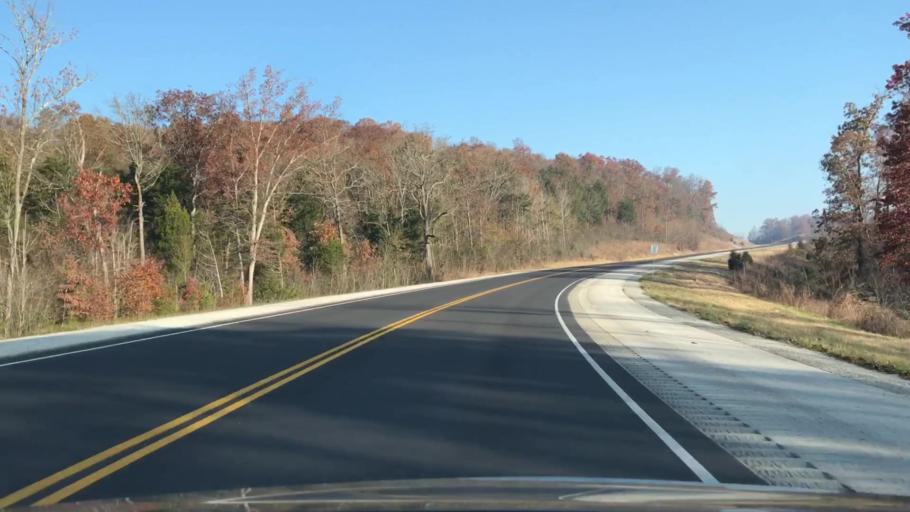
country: US
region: Kentucky
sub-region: Edmonson County
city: Brownsville
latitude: 37.0945
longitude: -86.2336
